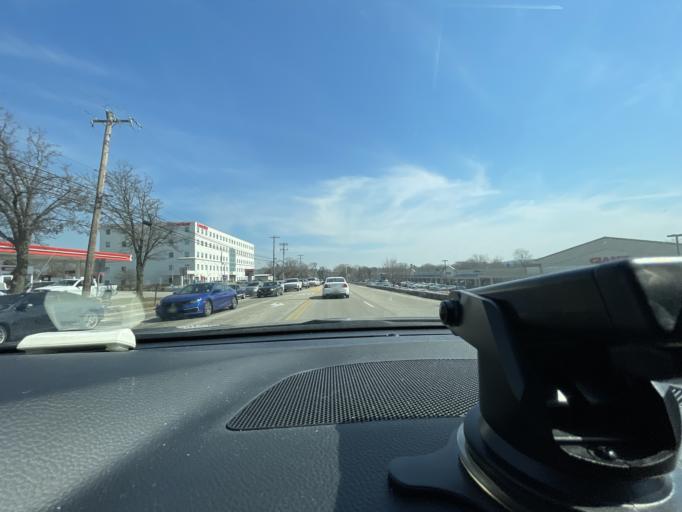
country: US
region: Pennsylvania
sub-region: Montgomery County
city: Plymouth Meeting
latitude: 40.0942
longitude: -75.2863
